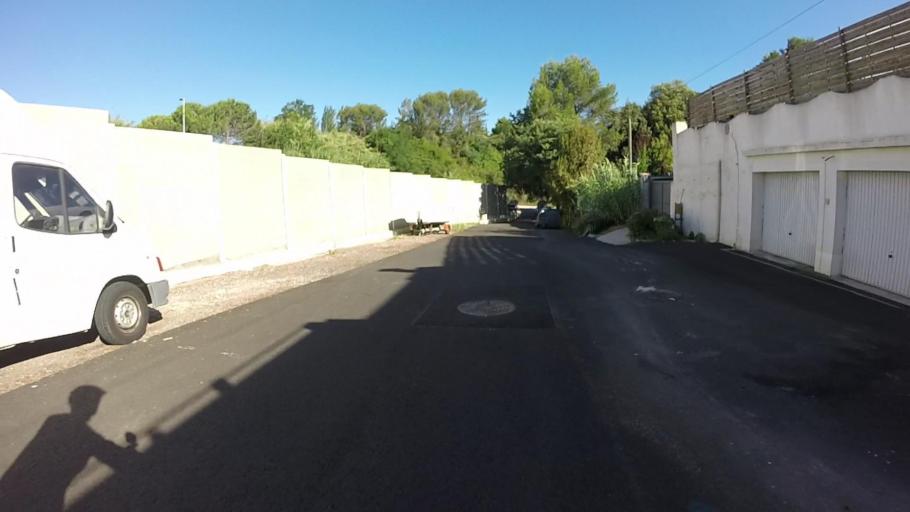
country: FR
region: Provence-Alpes-Cote d'Azur
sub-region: Departement des Alpes-Maritimes
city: Biot
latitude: 43.6052
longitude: 7.0825
